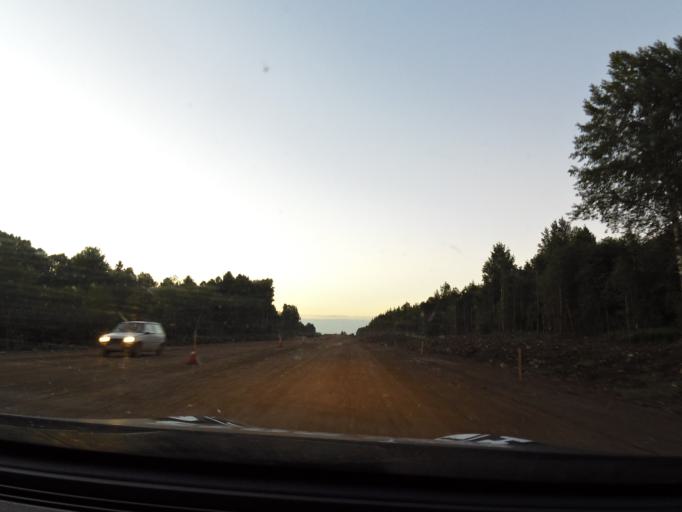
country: RU
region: Vologda
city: Vytegra
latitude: 60.9961
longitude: 36.1213
